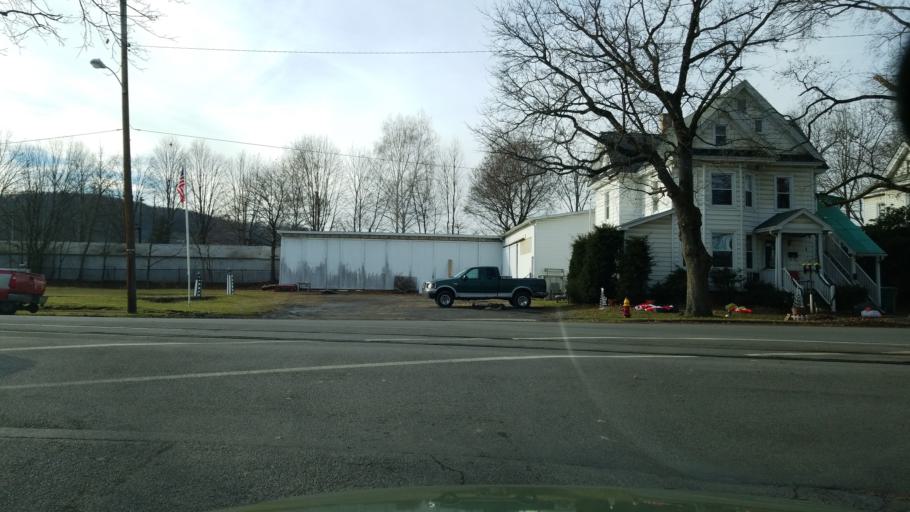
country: US
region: Pennsylvania
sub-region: Clearfield County
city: Clearfield
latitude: 41.0298
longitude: -78.4415
